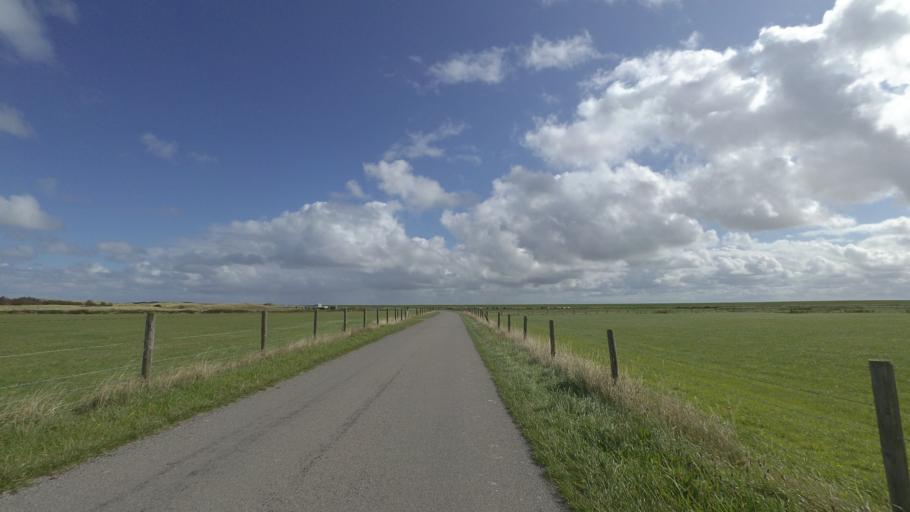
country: NL
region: Friesland
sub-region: Gemeente Ameland
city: Nes
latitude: 53.4487
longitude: 5.8397
